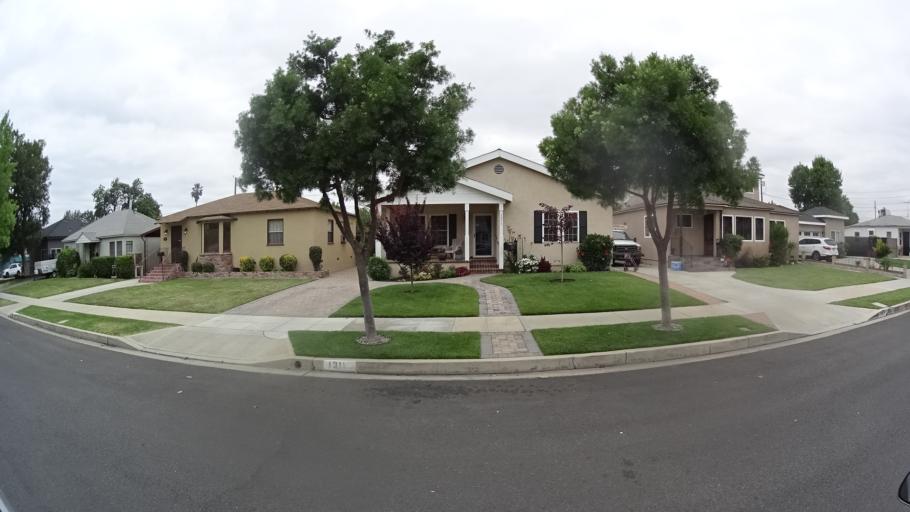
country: US
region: California
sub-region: Los Angeles County
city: Burbank
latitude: 34.1868
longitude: -118.3283
